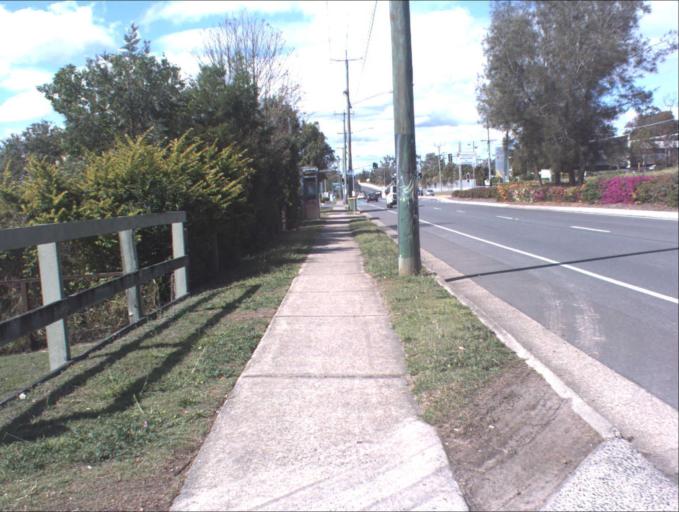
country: AU
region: Queensland
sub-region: Logan
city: Park Ridge South
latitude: -27.6751
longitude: 153.0269
